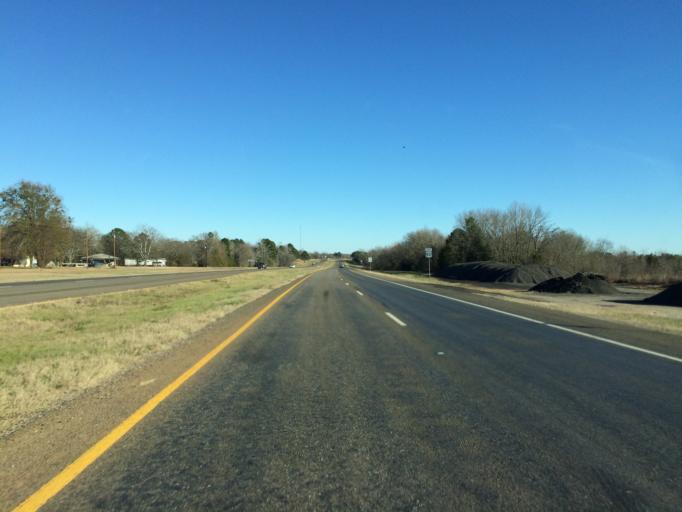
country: US
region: Texas
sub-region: Wood County
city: Hawkins
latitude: 32.6163
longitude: -95.3138
